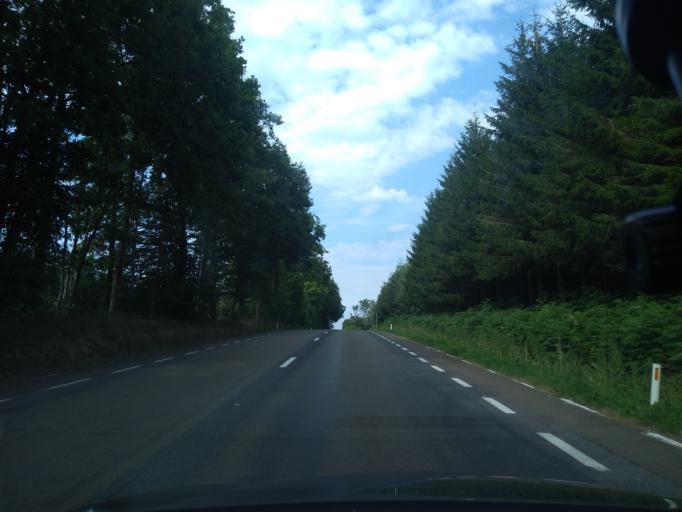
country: BE
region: Wallonia
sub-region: Province du Luxembourg
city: Libin
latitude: 49.9955
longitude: 5.2686
